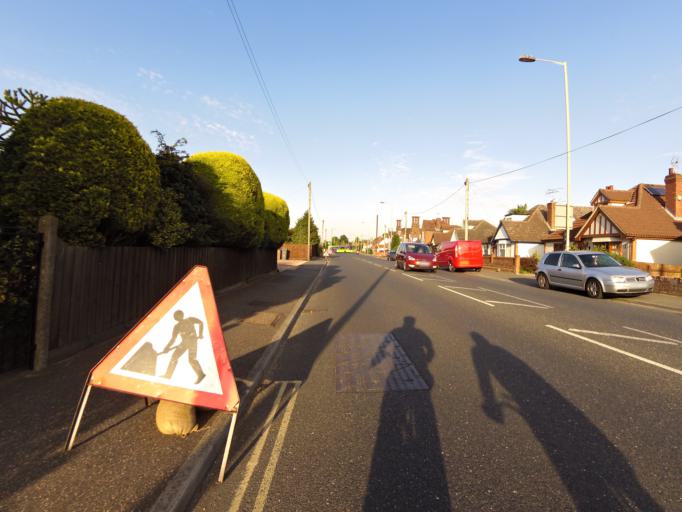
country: GB
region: England
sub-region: Suffolk
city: Kesgrave
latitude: 52.0492
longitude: 1.2105
